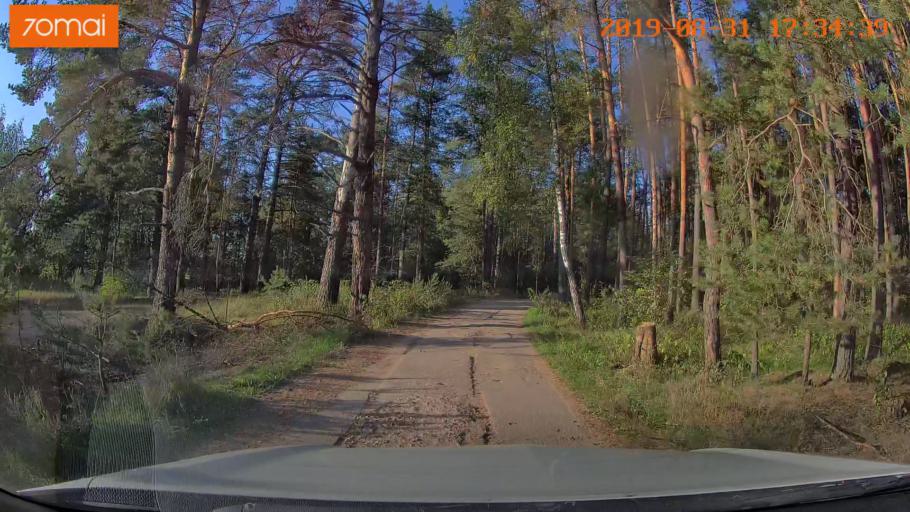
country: RU
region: Kaluga
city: Detchino
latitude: 54.8137
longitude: 36.3520
